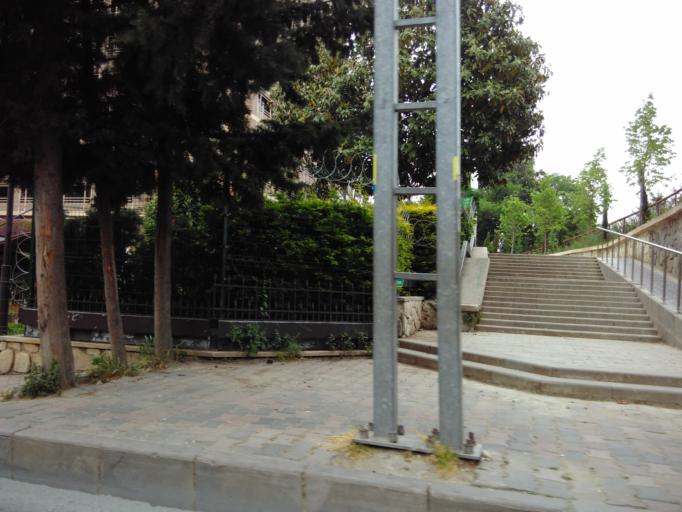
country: TR
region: Istanbul
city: Sisli
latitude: 41.0406
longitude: 28.9874
